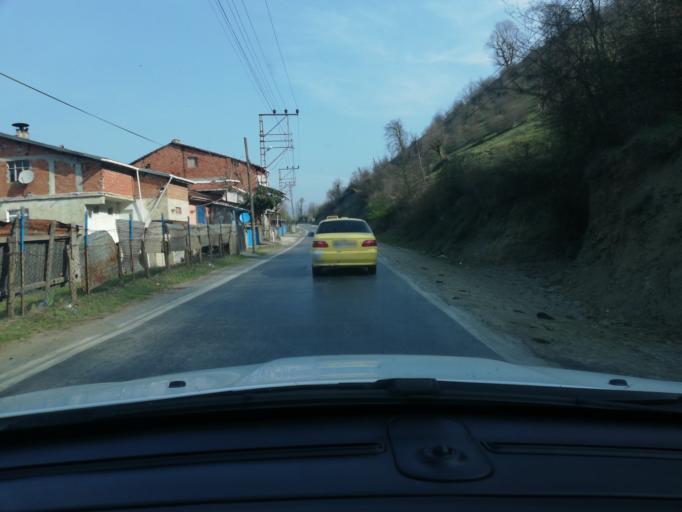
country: TR
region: Karabuk
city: Yenice
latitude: 41.2179
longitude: 32.3633
